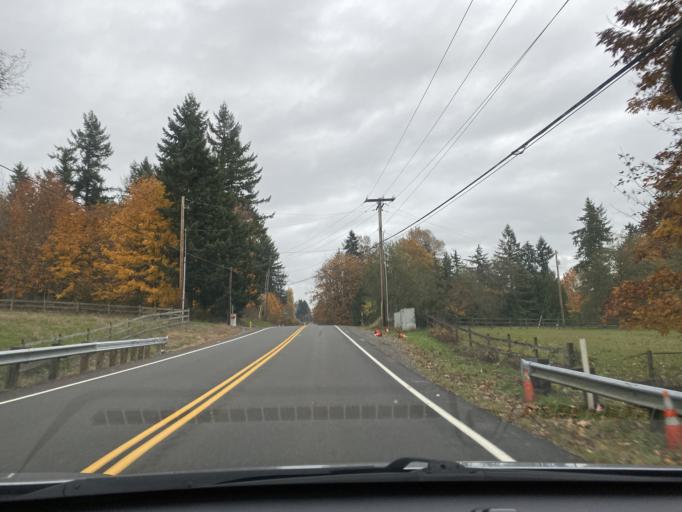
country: US
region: Washington
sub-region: King County
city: Lake Morton-Berrydale
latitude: 47.3007
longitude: -122.1390
